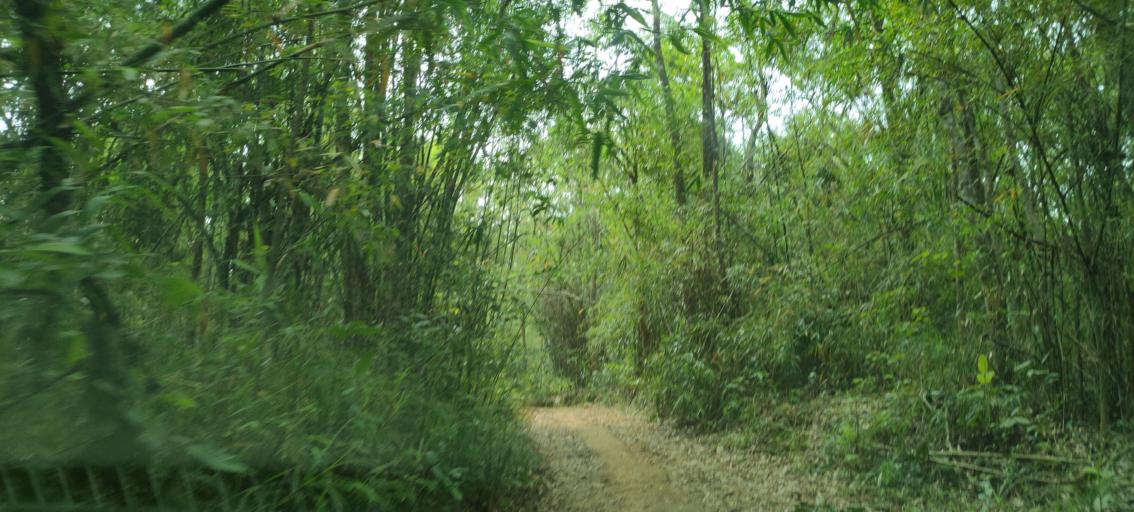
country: LA
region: Loungnamtha
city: Muang Nale
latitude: 20.4132
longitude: 101.4849
